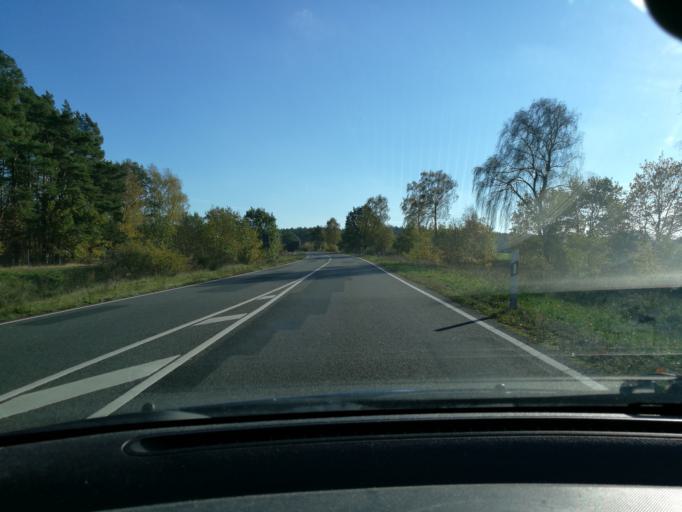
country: DE
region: Lower Saxony
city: Dahlem
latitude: 53.1767
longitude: 10.7680
